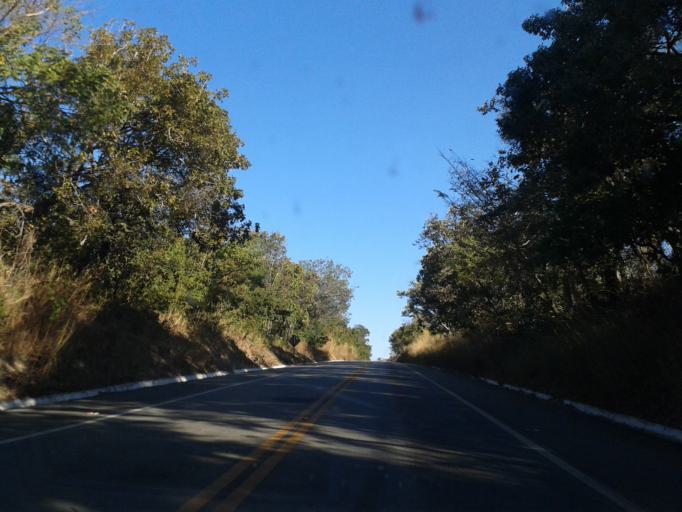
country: BR
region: Goias
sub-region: Itapuranga
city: Itapuranga
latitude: -15.5465
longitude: -50.2884
